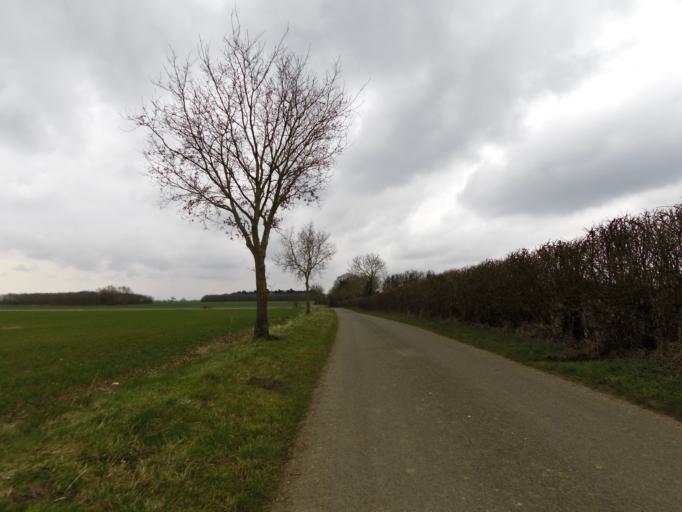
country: GB
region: England
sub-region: Suffolk
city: Halesworth
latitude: 52.3843
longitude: 1.5165
